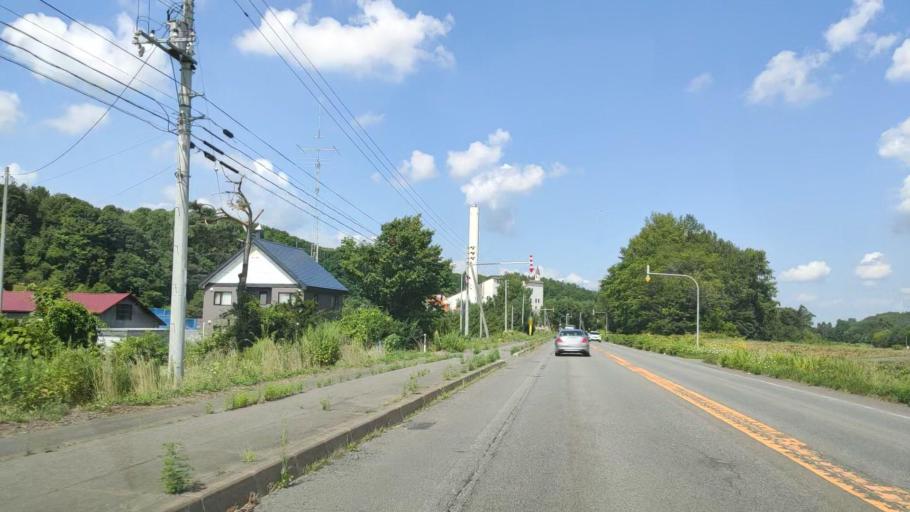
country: JP
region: Hokkaido
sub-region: Asahikawa-shi
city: Asahikawa
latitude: 43.6197
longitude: 142.4720
